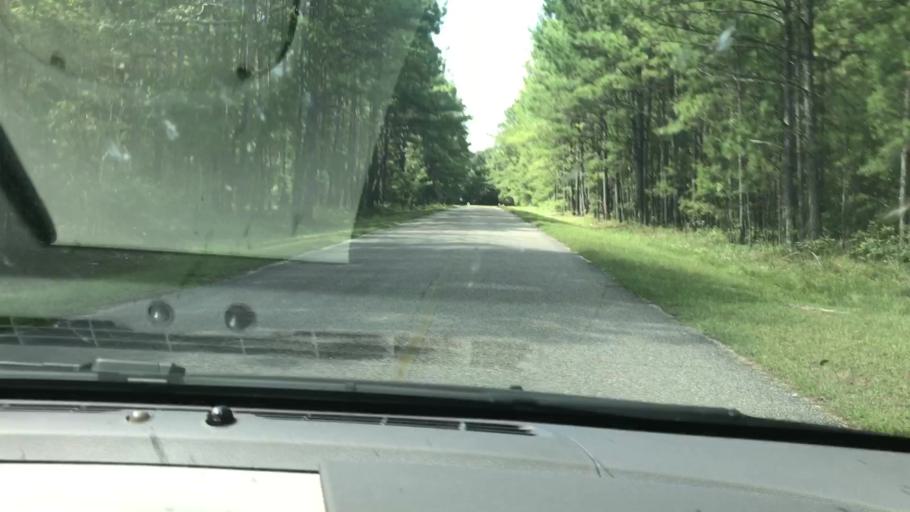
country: US
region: Georgia
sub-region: Clay County
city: Fort Gaines
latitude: 31.7439
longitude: -85.0787
